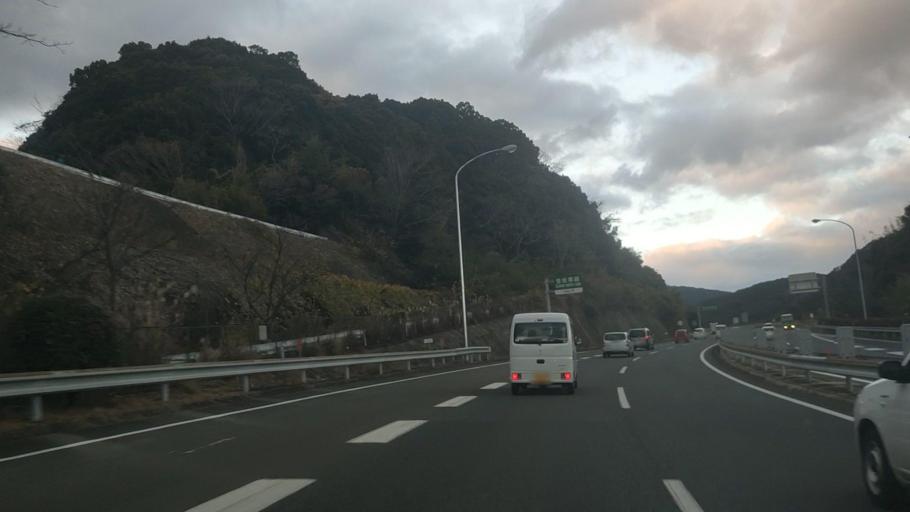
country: JP
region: Nagasaki
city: Obita
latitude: 32.8135
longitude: 129.9568
